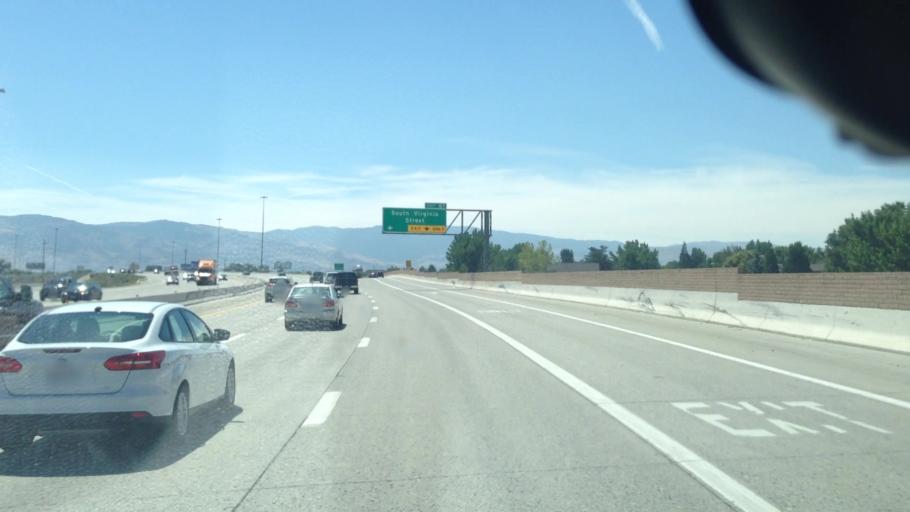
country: US
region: Nevada
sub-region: Washoe County
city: Reno
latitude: 39.4531
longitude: -119.7809
